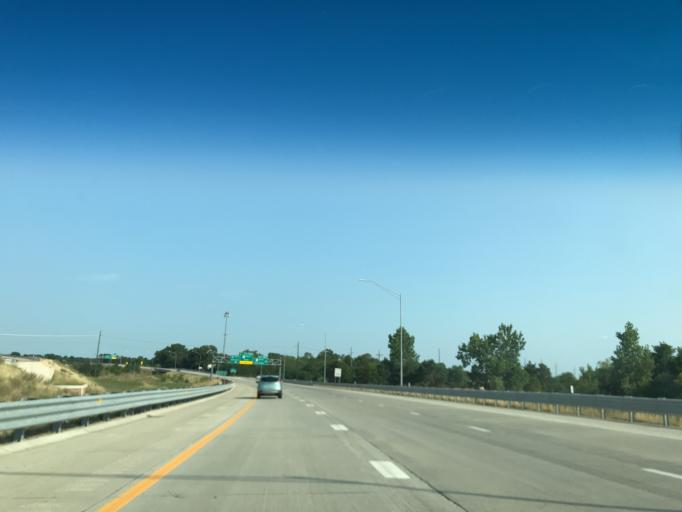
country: US
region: Michigan
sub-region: Livingston County
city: Brighton
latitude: 42.5259
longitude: -83.7613
